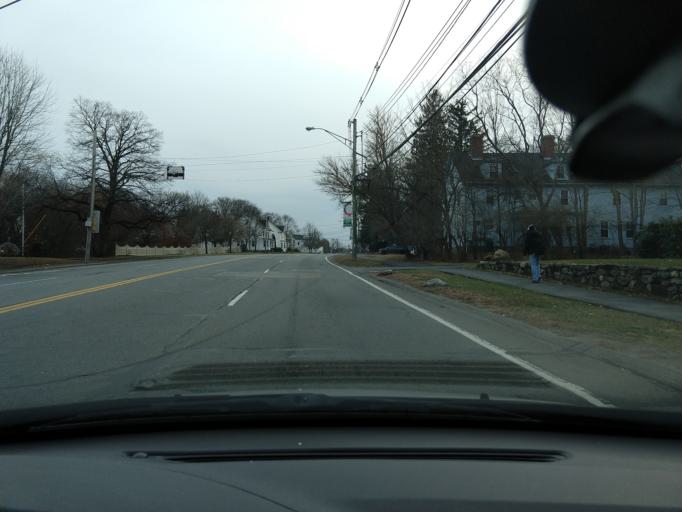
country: US
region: Massachusetts
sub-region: Middlesex County
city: Billerica
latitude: 42.5622
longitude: -71.2702
